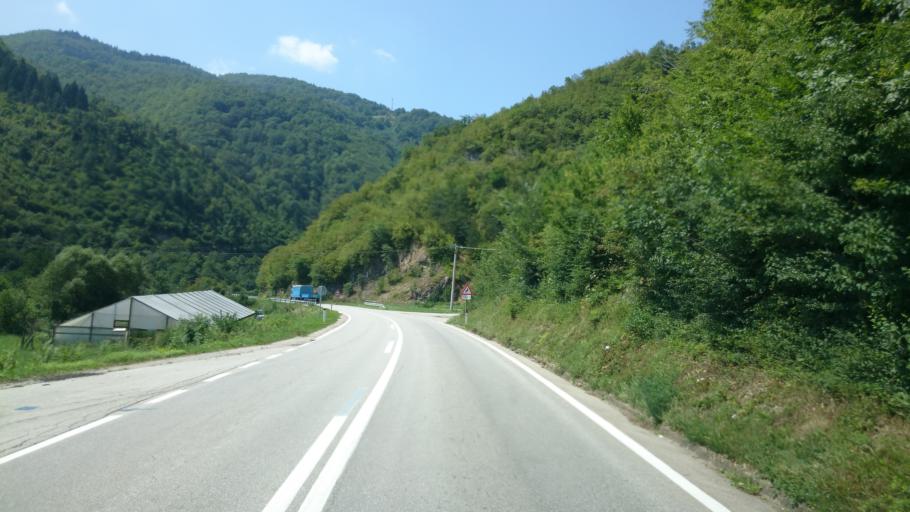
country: BA
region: Federation of Bosnia and Herzegovina
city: Donji Vakuf
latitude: 44.1847
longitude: 17.3479
